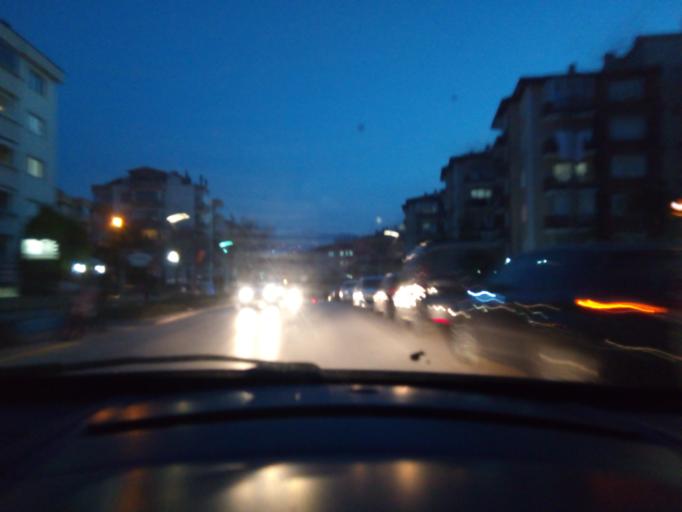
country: TR
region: Bursa
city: Yildirim
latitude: 40.2252
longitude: 28.9843
